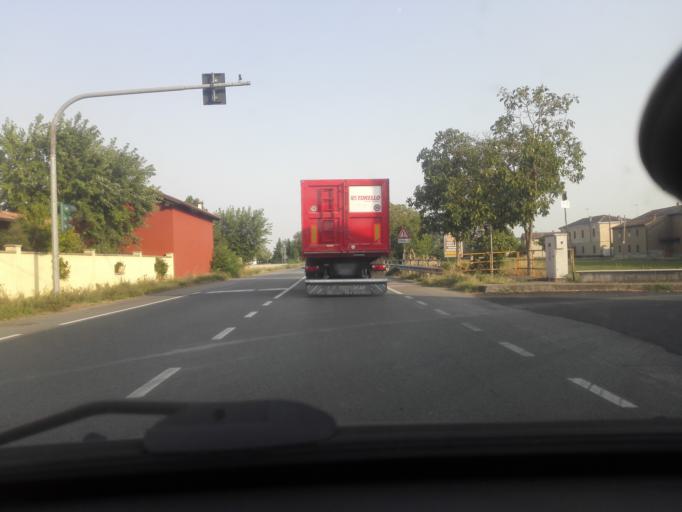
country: IT
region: Piedmont
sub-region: Provincia di Alessandria
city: Litta Parodi-Cascinagrossa
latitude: 44.8666
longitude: 8.7022
